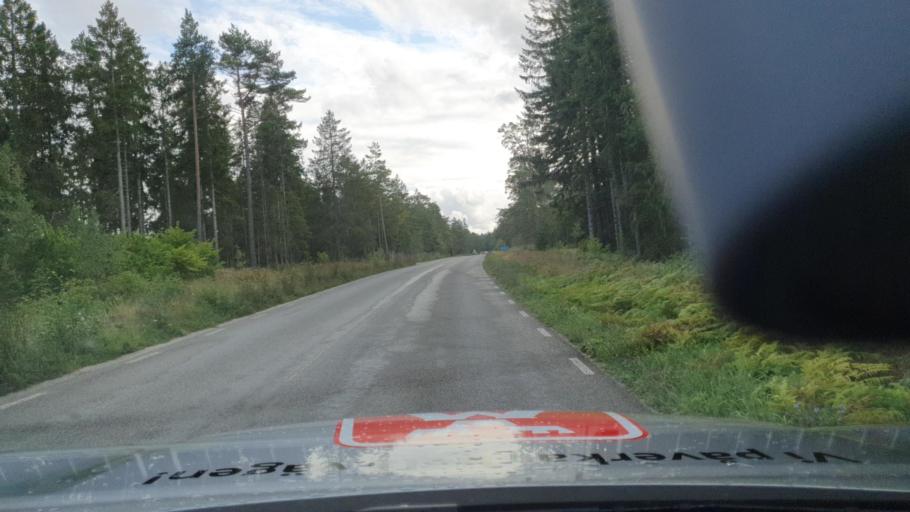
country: SE
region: Gotland
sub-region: Gotland
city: Slite
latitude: 57.6182
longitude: 18.7585
